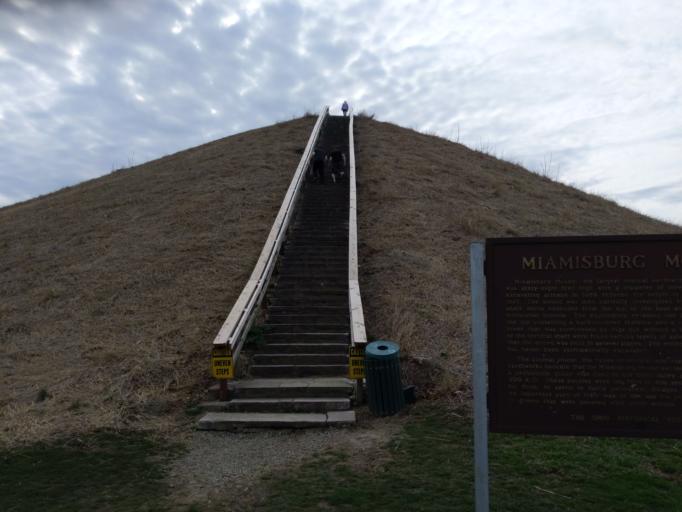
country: US
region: Ohio
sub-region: Montgomery County
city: Miamisburg
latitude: 39.6276
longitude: -84.2803
